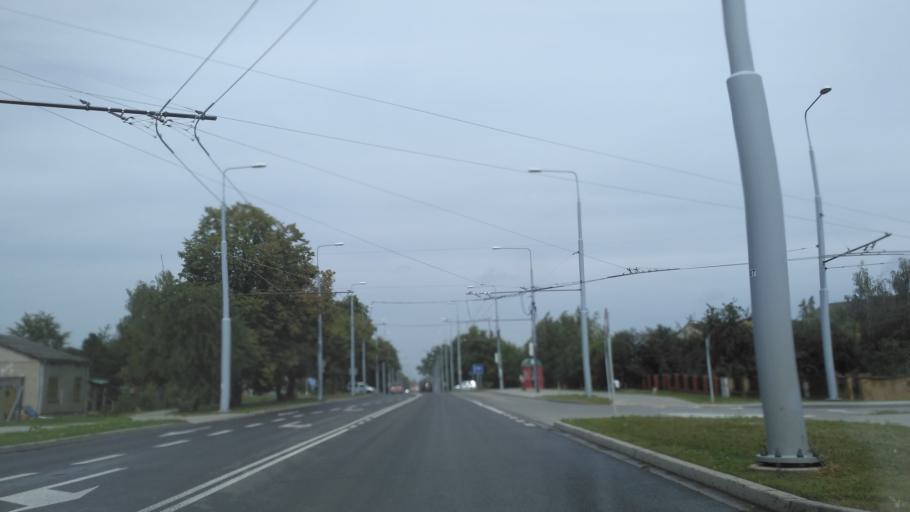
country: PL
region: Lublin Voivodeship
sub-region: Powiat lubelski
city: Lublin
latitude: 51.1968
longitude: 22.5860
